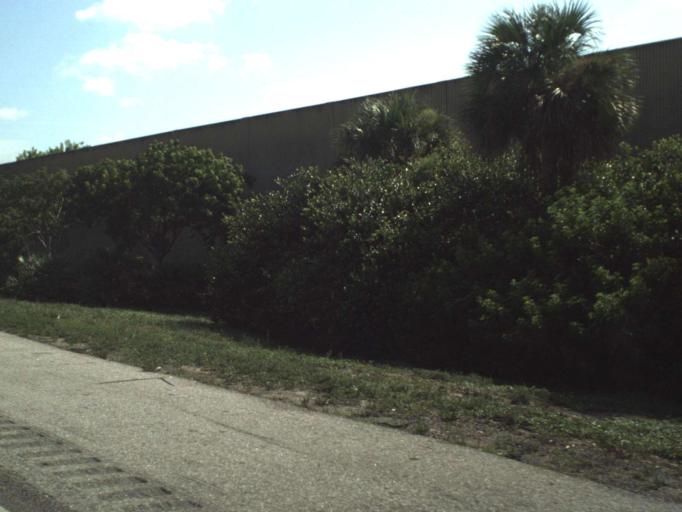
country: US
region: Florida
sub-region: Palm Beach County
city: Schall Circle
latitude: 26.7309
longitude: -80.0910
